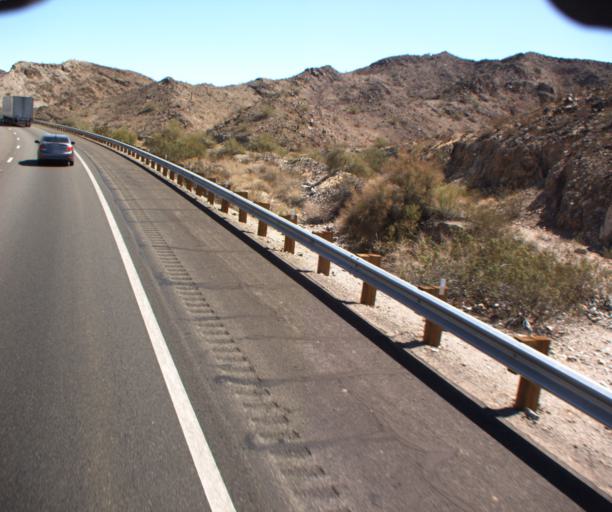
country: US
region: Arizona
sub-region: Yuma County
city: Fortuna Foothills
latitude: 32.6587
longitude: -114.3362
